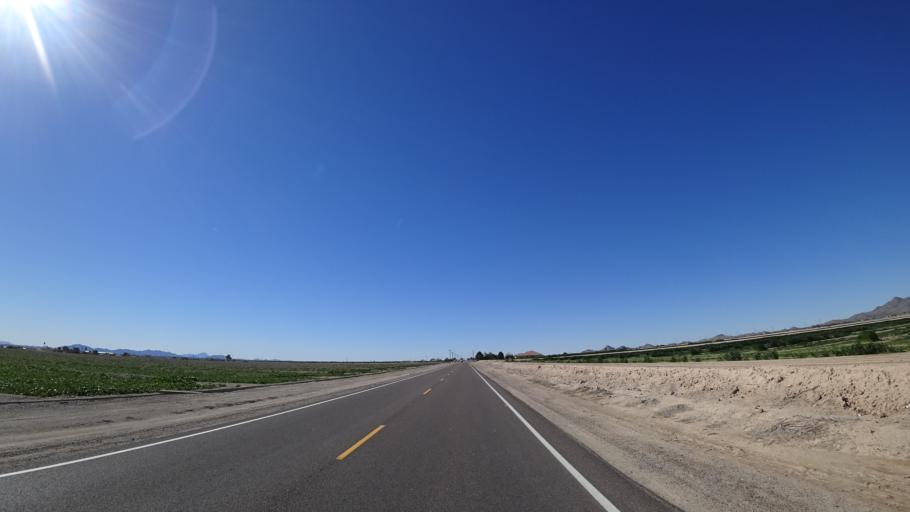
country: US
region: Arizona
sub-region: Maricopa County
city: Buckeye
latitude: 33.4068
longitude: -112.5332
